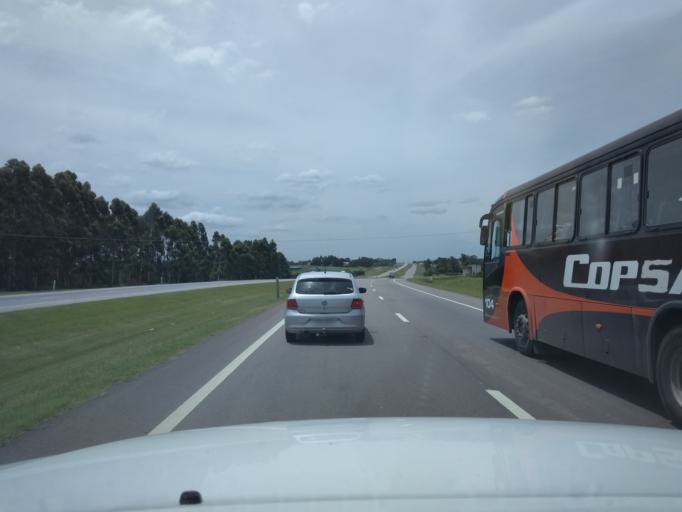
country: UY
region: Canelones
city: Progreso
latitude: -34.6841
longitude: -56.2406
